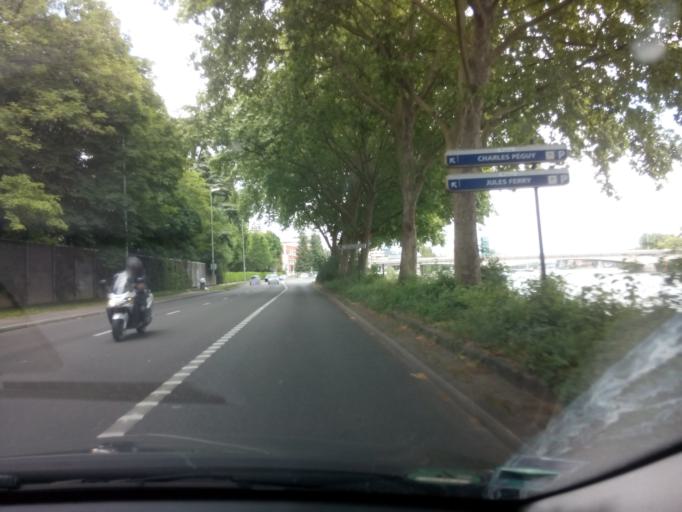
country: FR
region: Ile-de-France
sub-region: Departement des Hauts-de-Seine
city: Suresnes
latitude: 48.8634
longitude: 2.2274
